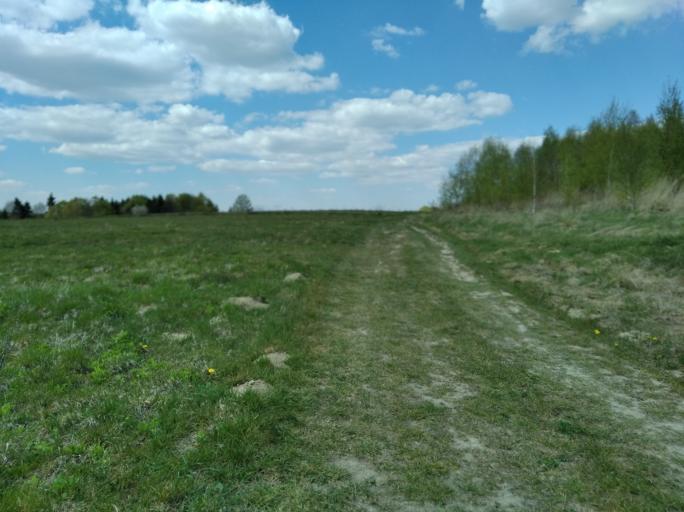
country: PL
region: Subcarpathian Voivodeship
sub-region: Powiat brzozowski
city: Golcowa
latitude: 49.7534
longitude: 22.0747
